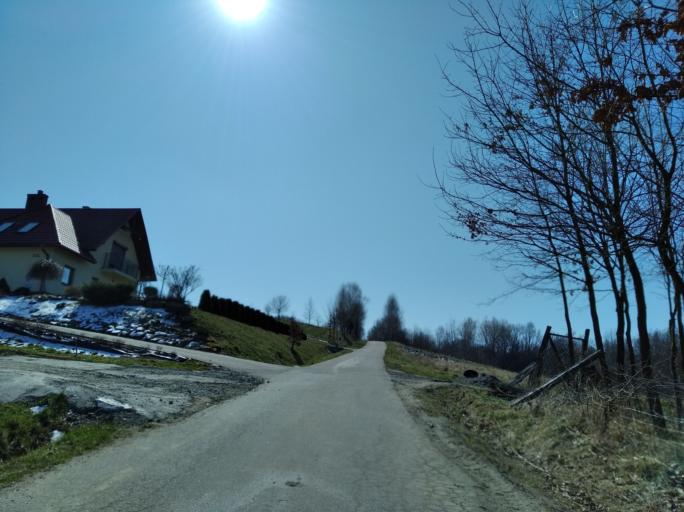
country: PL
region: Subcarpathian Voivodeship
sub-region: Powiat strzyzowski
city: Strzyzow
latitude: 49.8599
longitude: 21.8120
